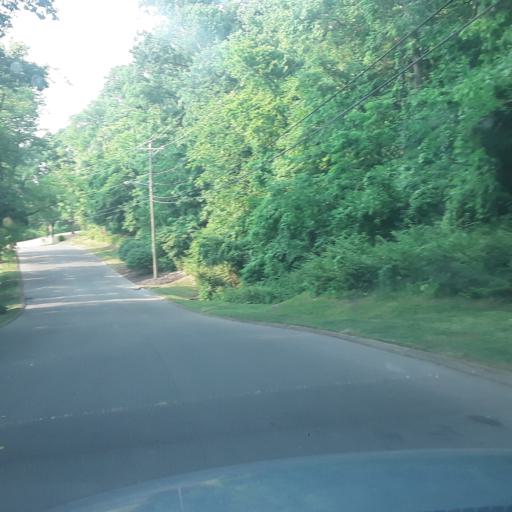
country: US
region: Tennessee
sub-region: Williamson County
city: Brentwood Estates
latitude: 36.0368
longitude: -86.7311
